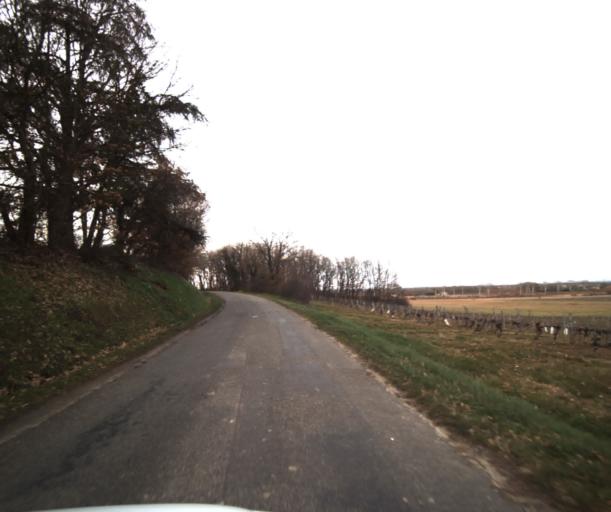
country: FR
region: Midi-Pyrenees
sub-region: Departement du Tarn-et-Garonne
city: Campsas
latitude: 43.8974
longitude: 1.3301
